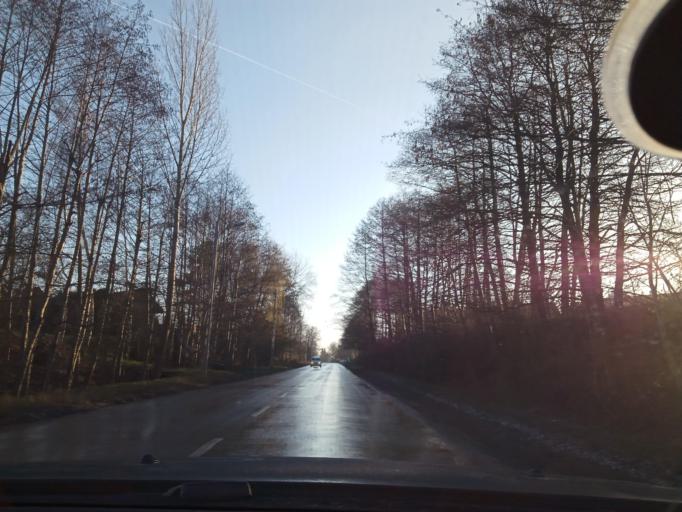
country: PL
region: Lesser Poland Voivodeship
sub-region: Powiat krakowski
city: Michalowice
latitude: 50.1047
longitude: 20.0549
